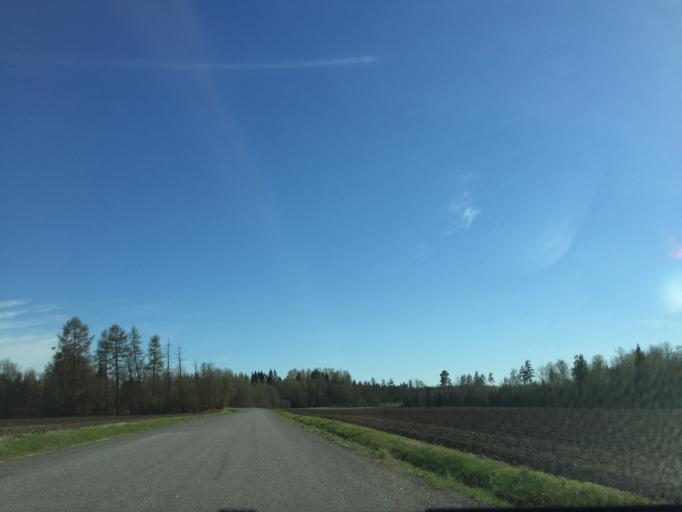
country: EE
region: Valgamaa
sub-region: Valga linn
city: Valga
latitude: 57.8533
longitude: 26.2534
